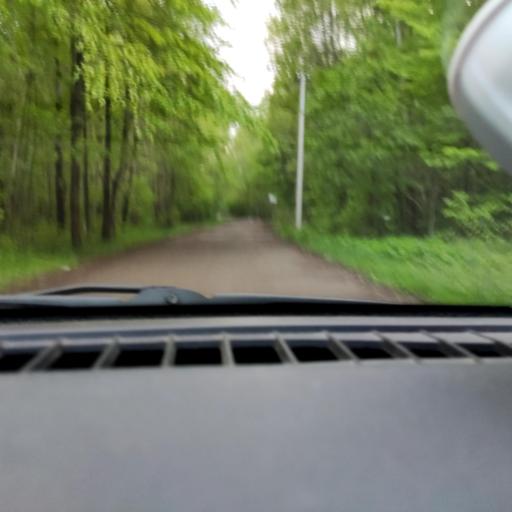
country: RU
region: Perm
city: Perm
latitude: 58.0809
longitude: 56.3831
